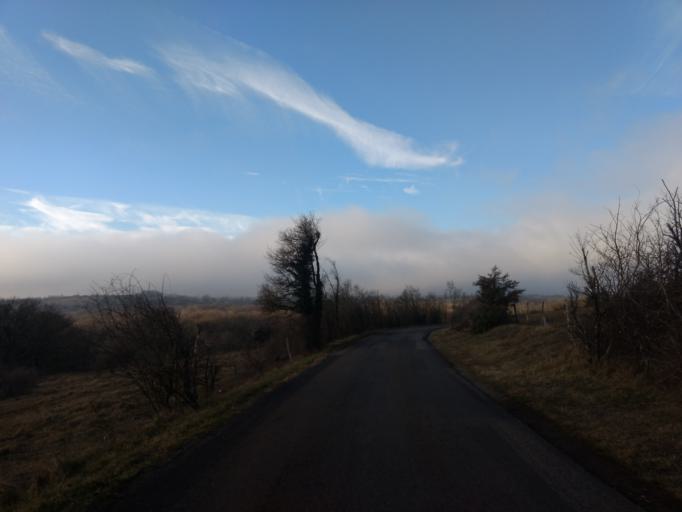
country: FR
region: Midi-Pyrenees
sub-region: Departement de l'Aveyron
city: Salles-la-Source
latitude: 44.4419
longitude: 2.5233
